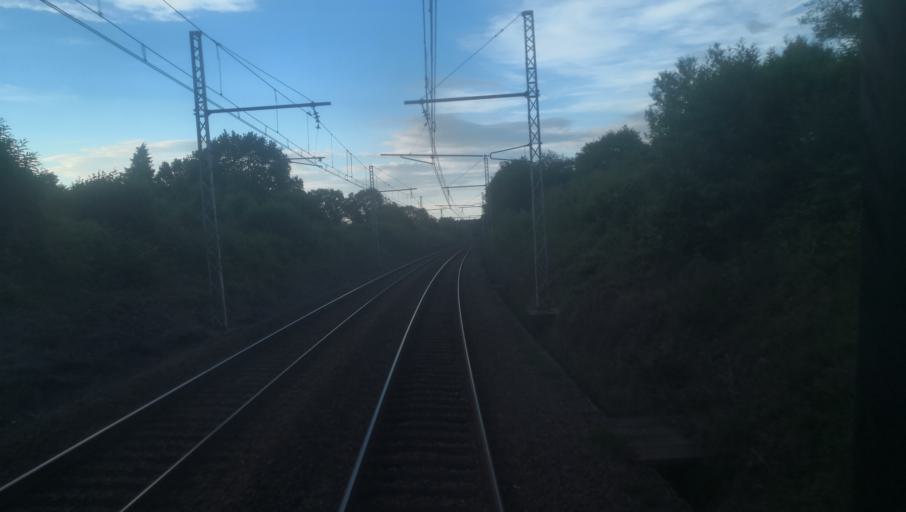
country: FR
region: Centre
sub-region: Departement de l'Indre
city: Chantome
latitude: 46.3709
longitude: 1.5371
